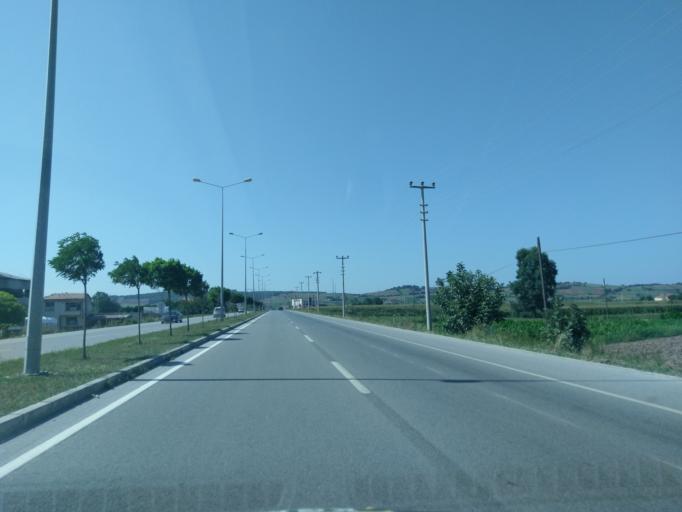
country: TR
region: Samsun
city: Bafra
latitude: 41.5739
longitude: 35.8654
